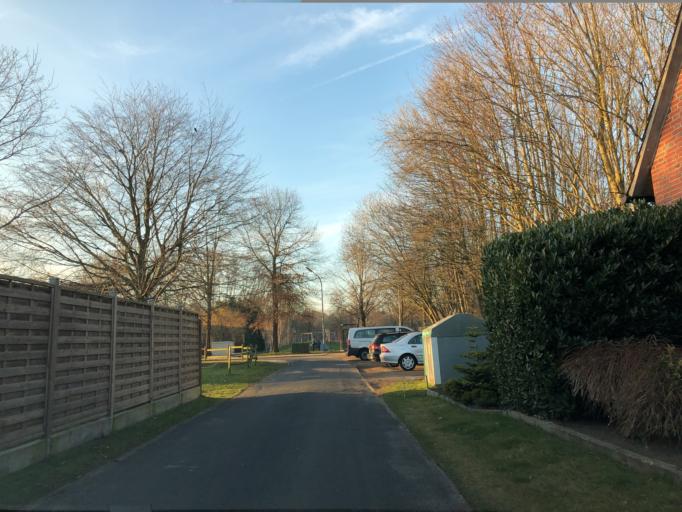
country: DE
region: Lower Saxony
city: Papenburg
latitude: 53.0799
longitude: 7.3850
